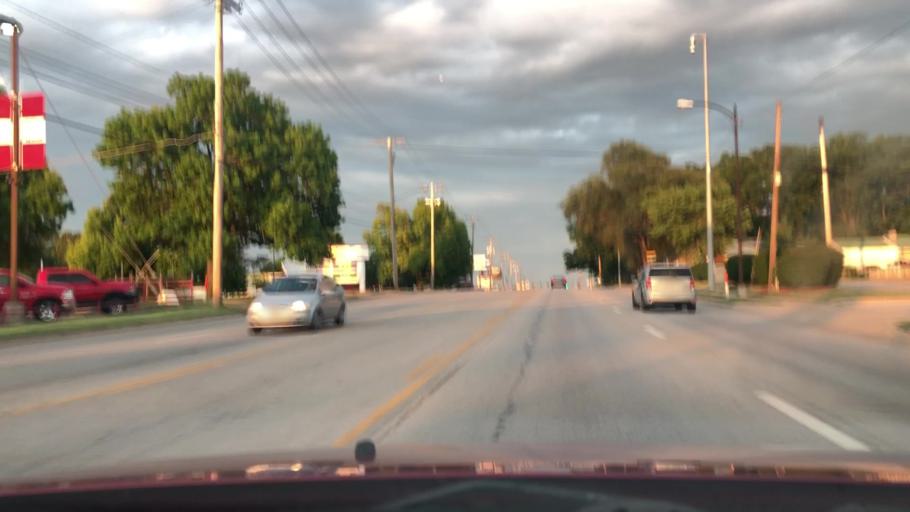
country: US
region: Missouri
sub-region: Greene County
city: Springfield
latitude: 37.1823
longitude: -93.3045
